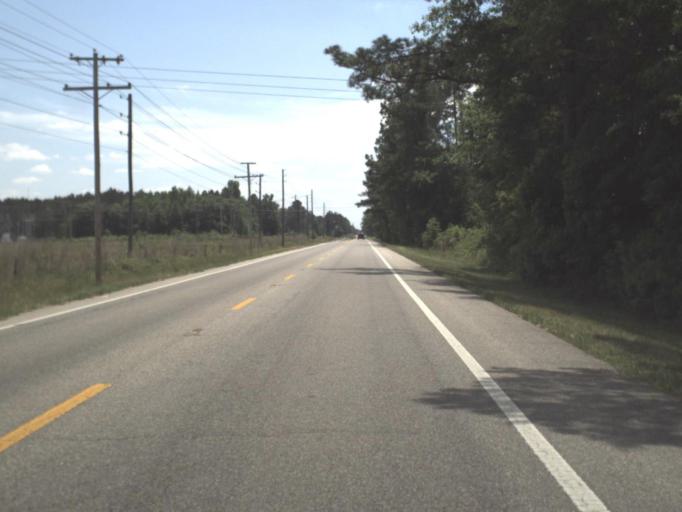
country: US
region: Florida
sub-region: Calhoun County
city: Blountstown
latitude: 30.5175
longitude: -85.1256
